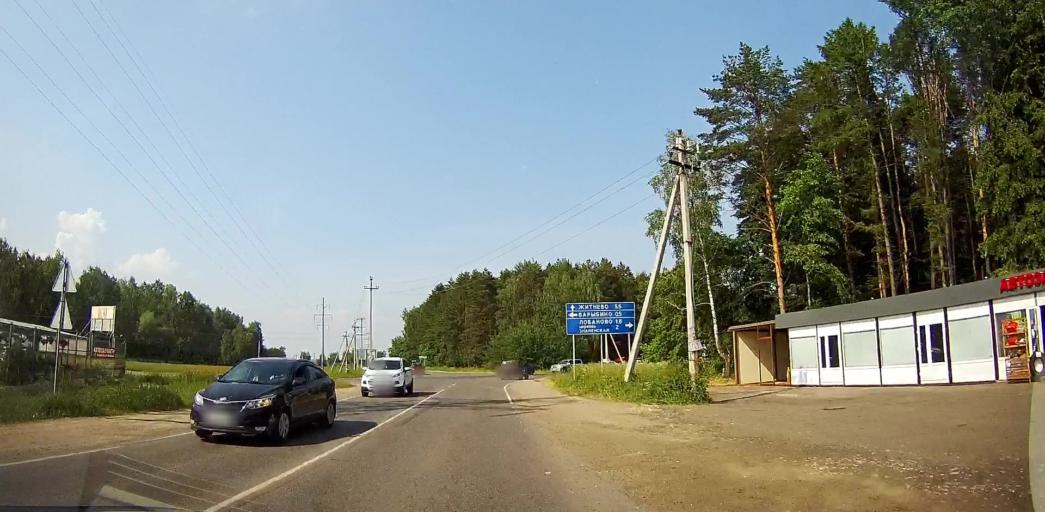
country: RU
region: Moskovskaya
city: Barybino
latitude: 55.2806
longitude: 37.9167
